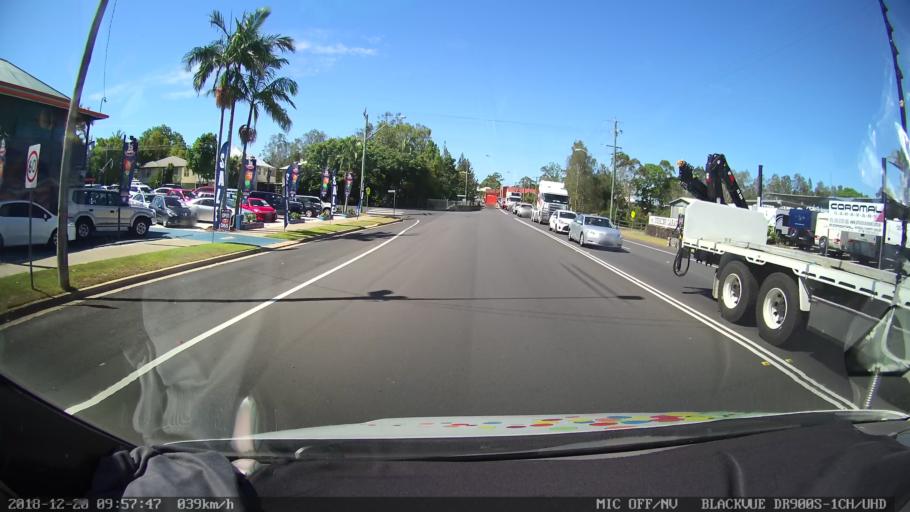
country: AU
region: New South Wales
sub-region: Lismore Municipality
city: Lismore
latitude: -28.8130
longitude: 153.2670
